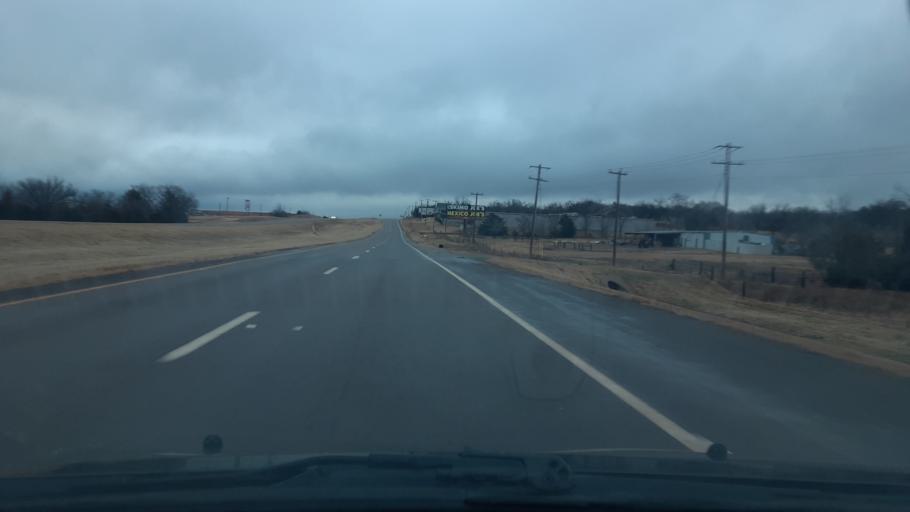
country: US
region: Oklahoma
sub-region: Payne County
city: Stillwater
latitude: 36.1159
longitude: -97.1726
